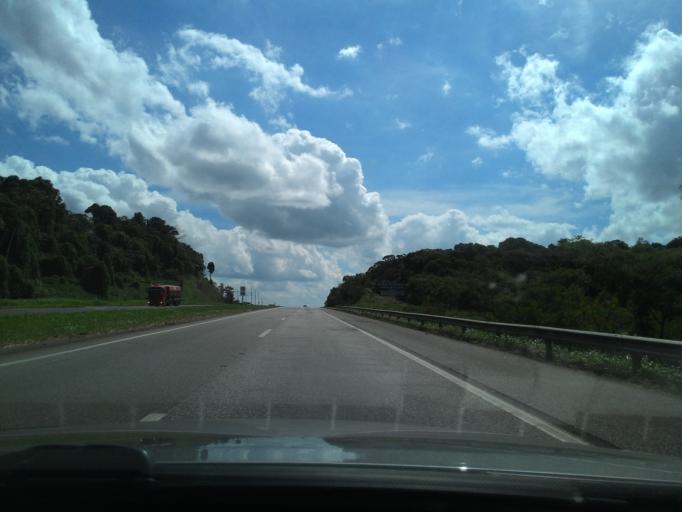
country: BR
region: Sao Paulo
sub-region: Jacupiranga
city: Jacupiranga
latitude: -24.6500
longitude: -47.9366
